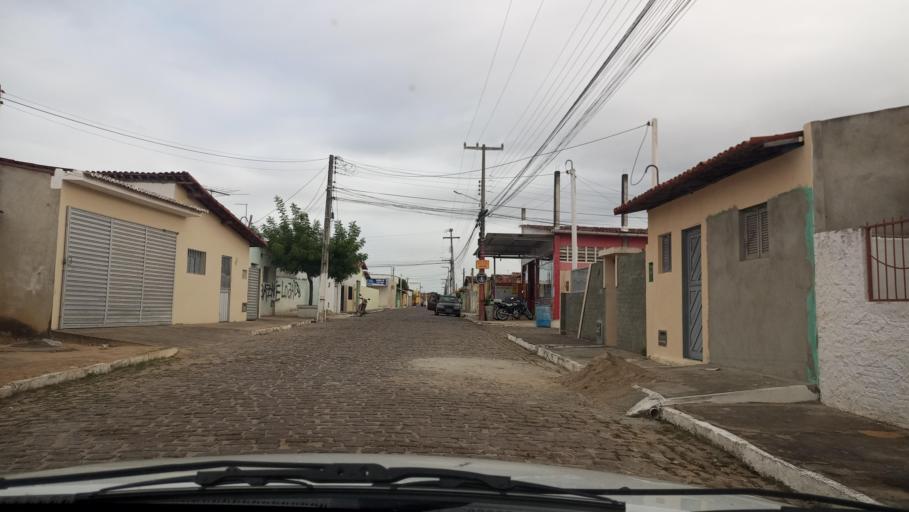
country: BR
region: Rio Grande do Norte
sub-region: Brejinho
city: Brejinho
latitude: -6.0463
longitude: -35.4324
